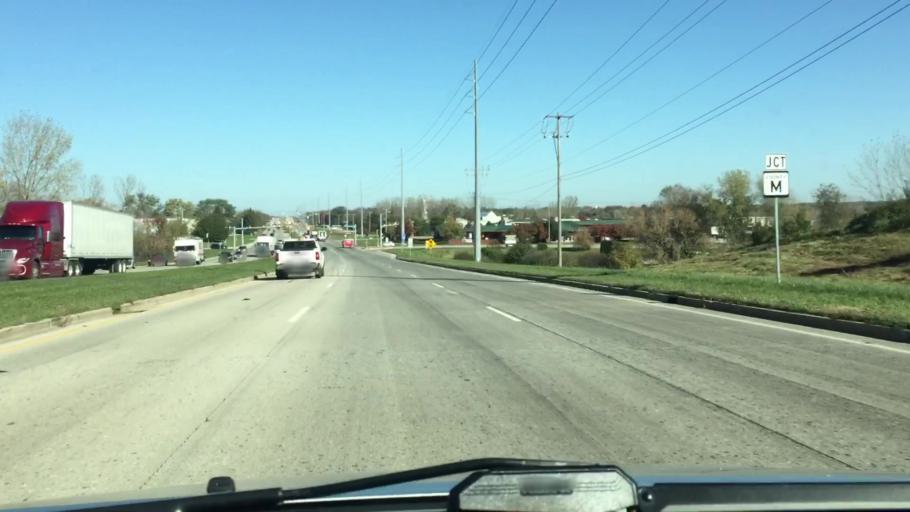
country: US
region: Wisconsin
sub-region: Waukesha County
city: Waukesha
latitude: 43.0566
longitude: -88.2056
